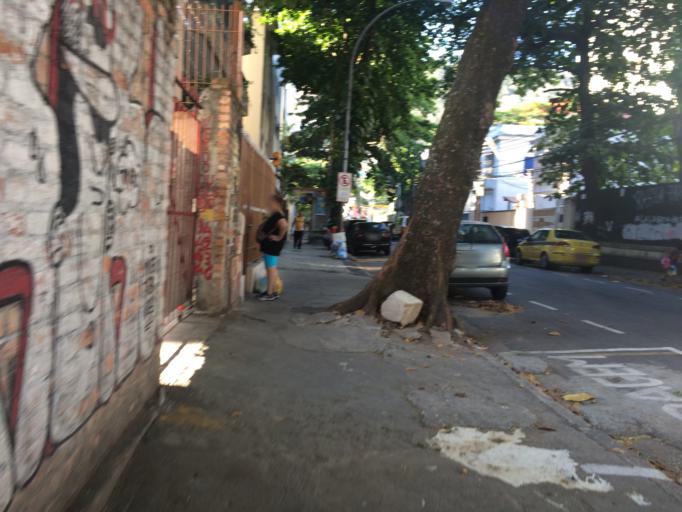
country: BR
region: Rio de Janeiro
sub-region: Rio De Janeiro
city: Rio de Janeiro
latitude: -22.9525
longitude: -43.1921
